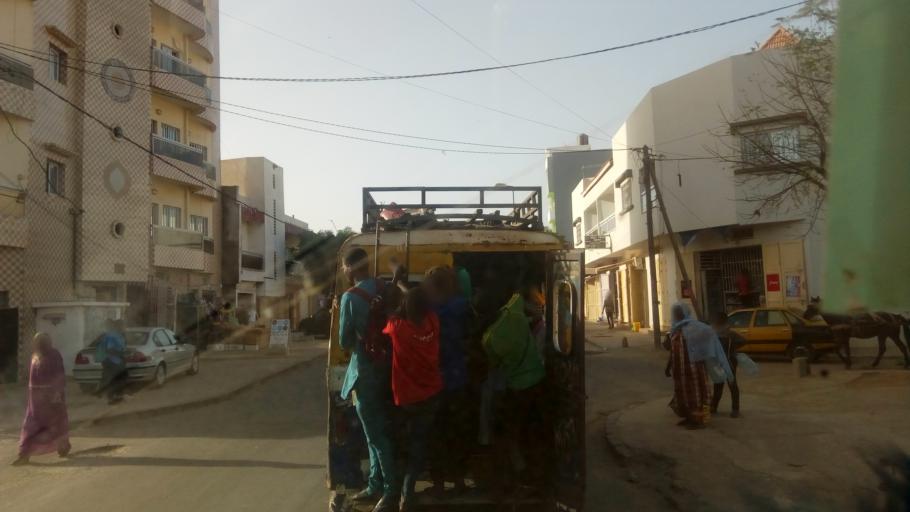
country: SN
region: Dakar
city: Grand Dakar
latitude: 14.7059
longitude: -17.4481
